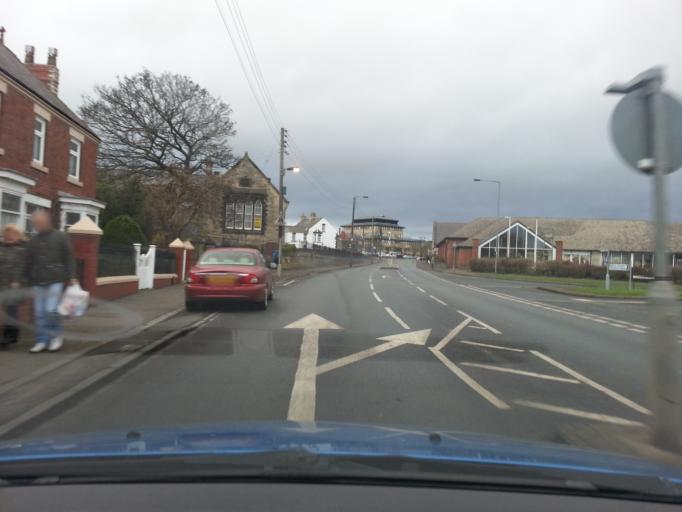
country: GB
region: England
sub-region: County Durham
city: Crook
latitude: 54.7125
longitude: -1.7464
